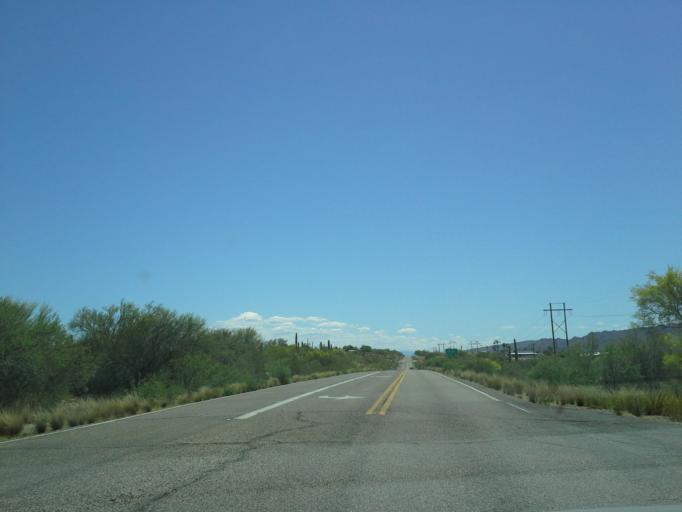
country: US
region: Arizona
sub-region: Pinal County
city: Kearny
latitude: 33.0657
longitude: -110.9114
